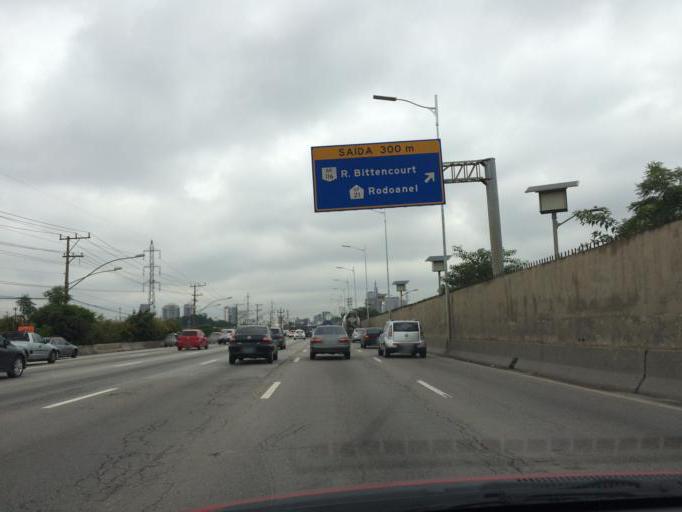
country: BR
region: Sao Paulo
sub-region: Osasco
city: Osasco
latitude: -23.5564
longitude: -46.7171
